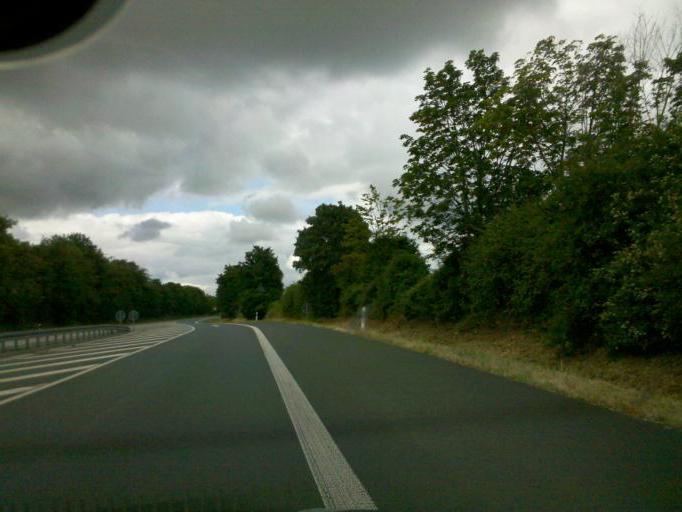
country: DE
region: North Rhine-Westphalia
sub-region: Regierungsbezirk Arnsberg
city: Anrochte
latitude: 51.5729
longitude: 8.3103
